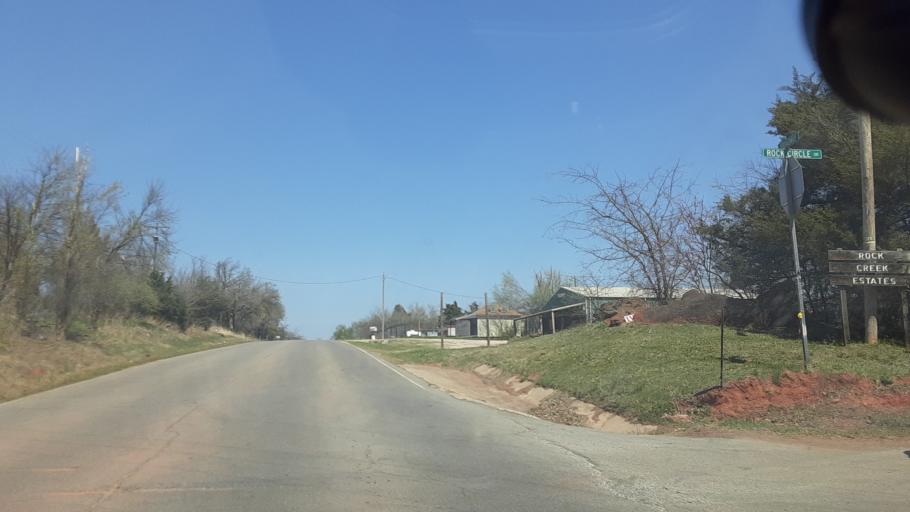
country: US
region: Oklahoma
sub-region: Oklahoma County
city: Edmond
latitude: 35.7575
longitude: -97.4784
